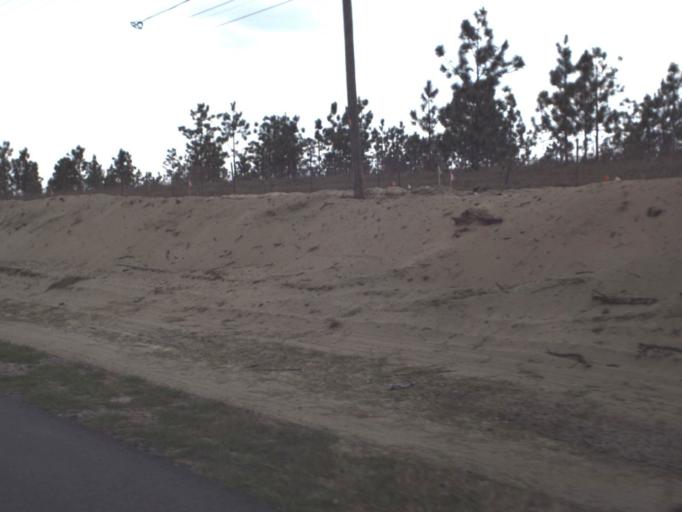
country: US
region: Florida
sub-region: Lake County
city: Clermont
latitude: 28.4409
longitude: -81.7173
